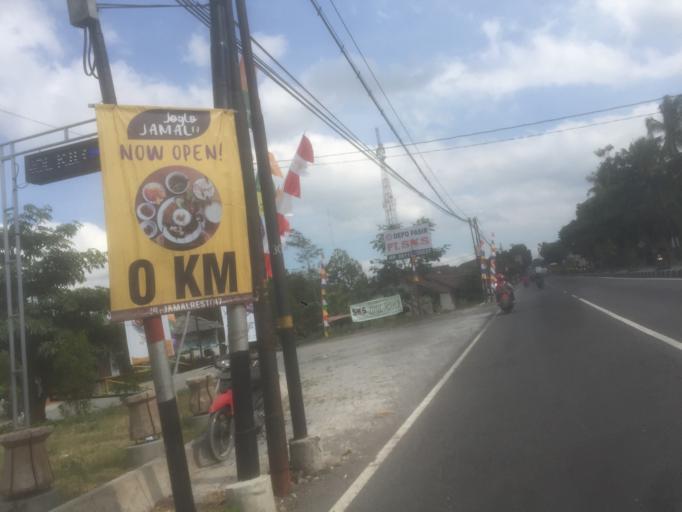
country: ID
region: Daerah Istimewa Yogyakarta
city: Sleman
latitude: -7.6662
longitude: 110.3315
